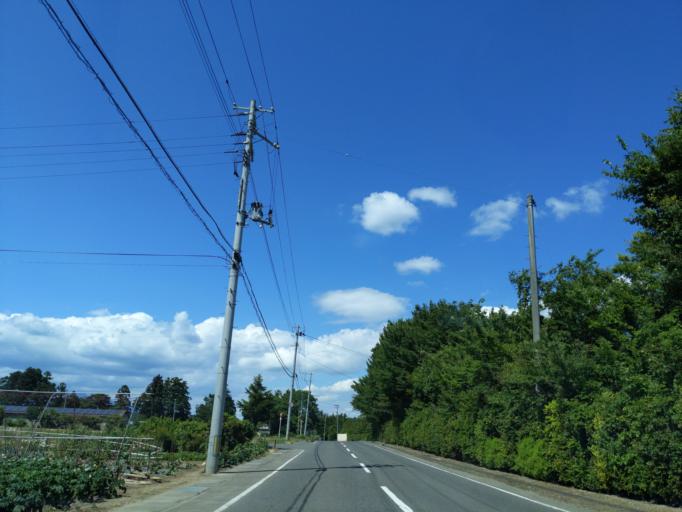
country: JP
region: Fukushima
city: Koriyama
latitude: 37.3932
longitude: 140.2666
